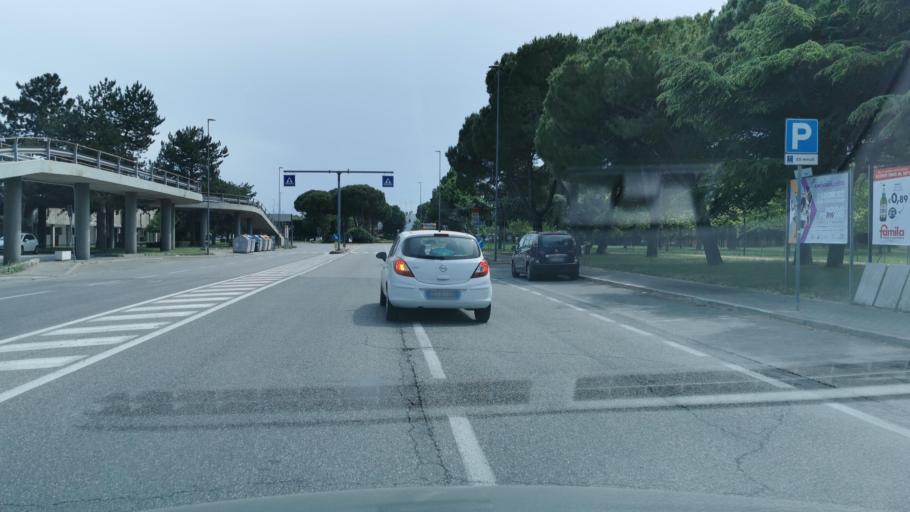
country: IT
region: Emilia-Romagna
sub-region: Provincia di Ravenna
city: Ravenna
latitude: 44.4244
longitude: 12.1824
